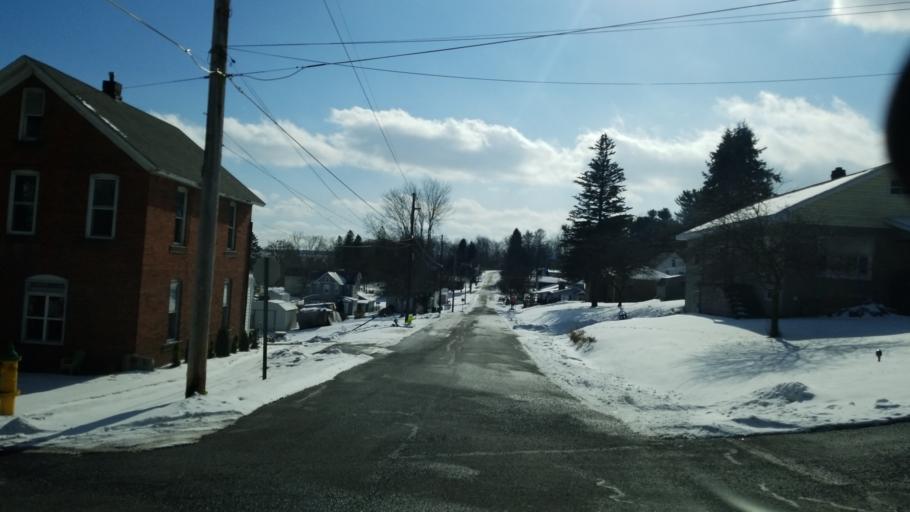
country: US
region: Pennsylvania
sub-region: Jefferson County
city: Falls Creek
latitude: 41.1413
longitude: -78.8064
